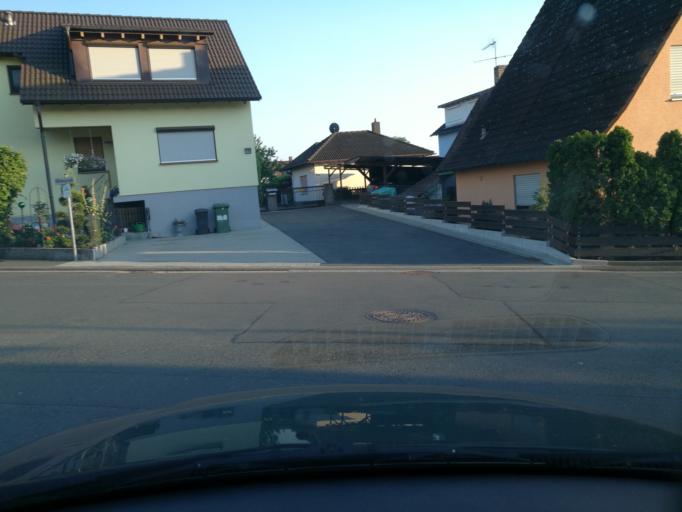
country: DE
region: Bavaria
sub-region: Regierungsbezirk Mittelfranken
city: Rottenbach
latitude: 49.6636
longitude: 10.9255
